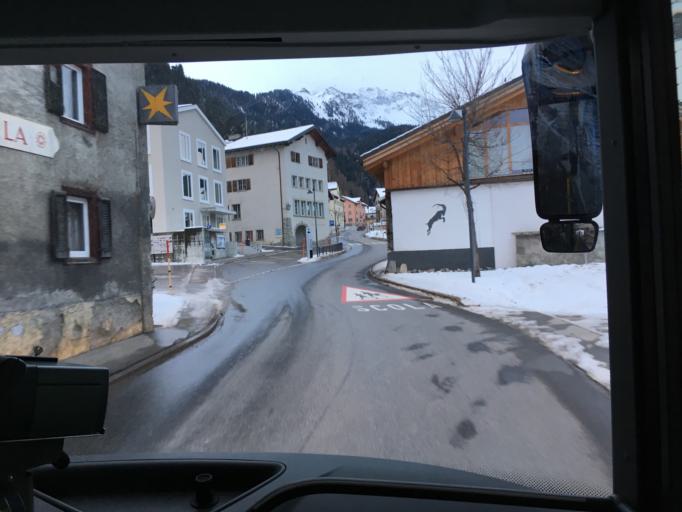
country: CH
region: Grisons
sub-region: Albula District
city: Tiefencastel
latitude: 46.5835
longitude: 9.6161
